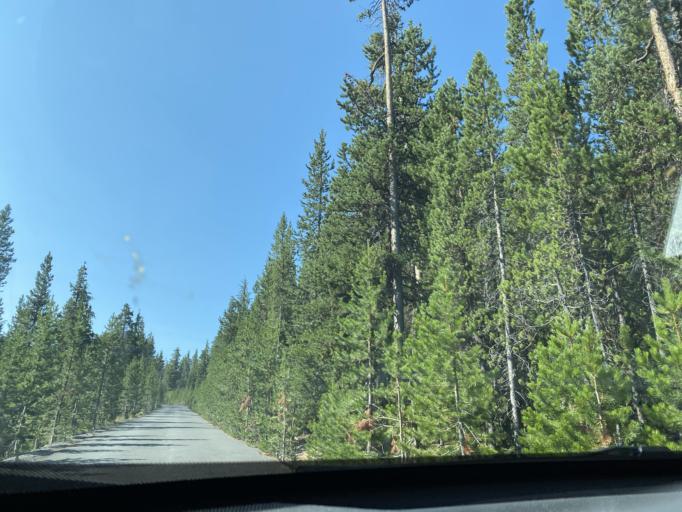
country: US
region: Oregon
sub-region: Deschutes County
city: Three Rivers
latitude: 43.7085
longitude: -121.2747
